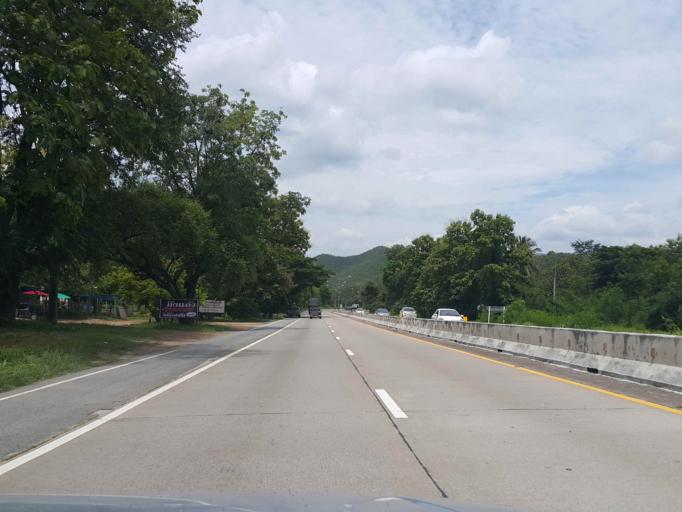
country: TH
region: Lamphun
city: Mae Tha
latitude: 18.5088
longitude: 99.1222
